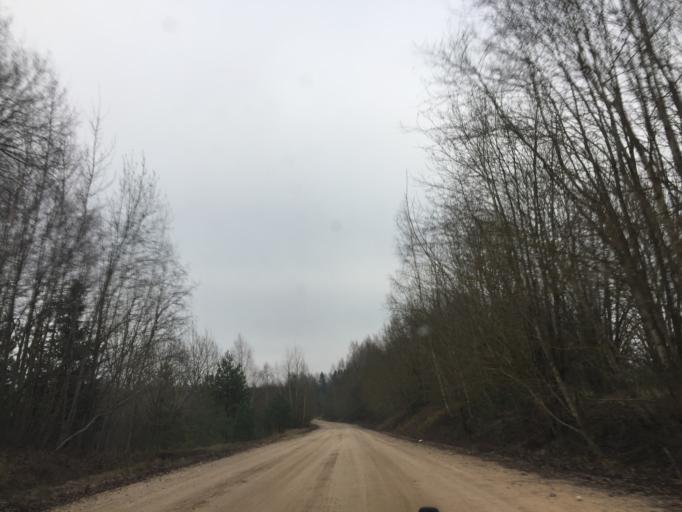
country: LV
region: Limbazu Rajons
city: Limbazi
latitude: 57.5969
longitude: 24.6172
